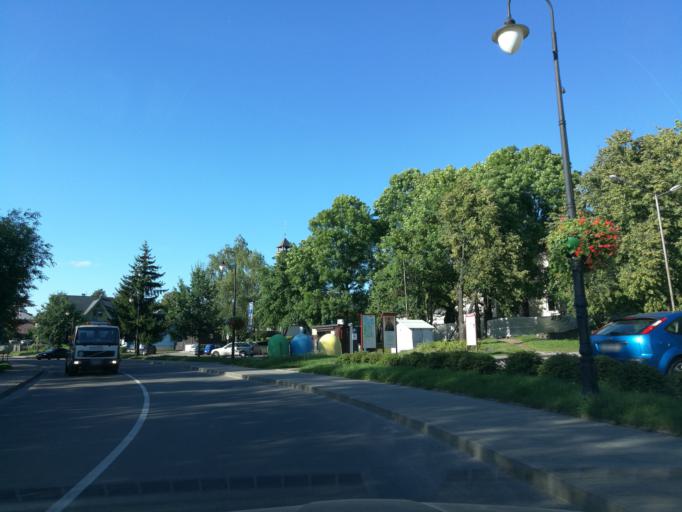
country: LT
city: Trakai
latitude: 54.6452
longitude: 24.9340
